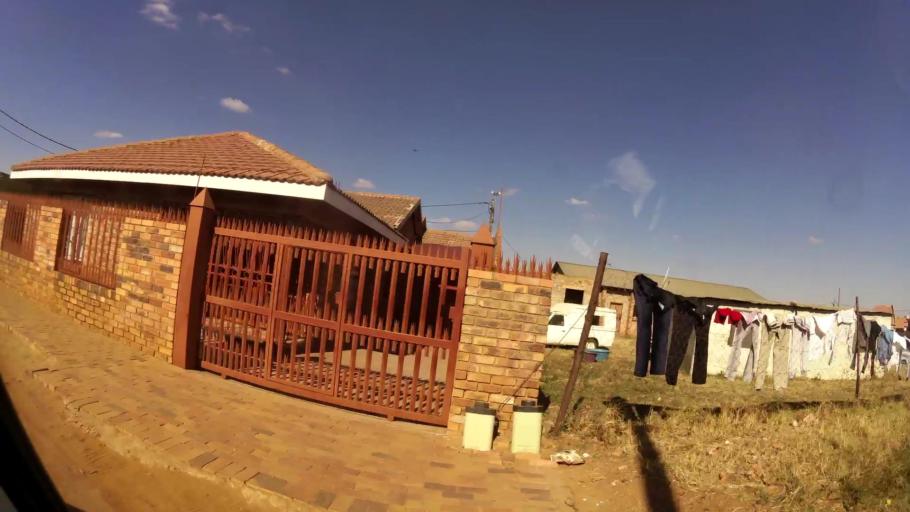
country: ZA
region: Gauteng
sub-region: City of Tshwane Metropolitan Municipality
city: Cullinan
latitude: -25.7129
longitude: 28.3923
